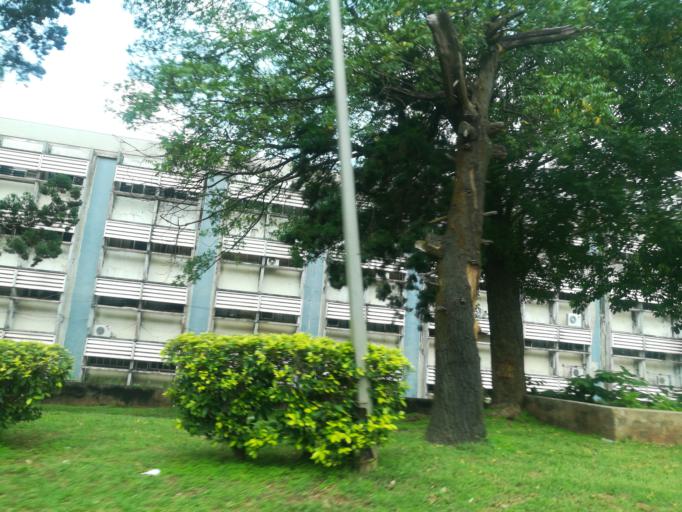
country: NG
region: Oyo
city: Ibadan
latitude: 7.4098
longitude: 3.9056
